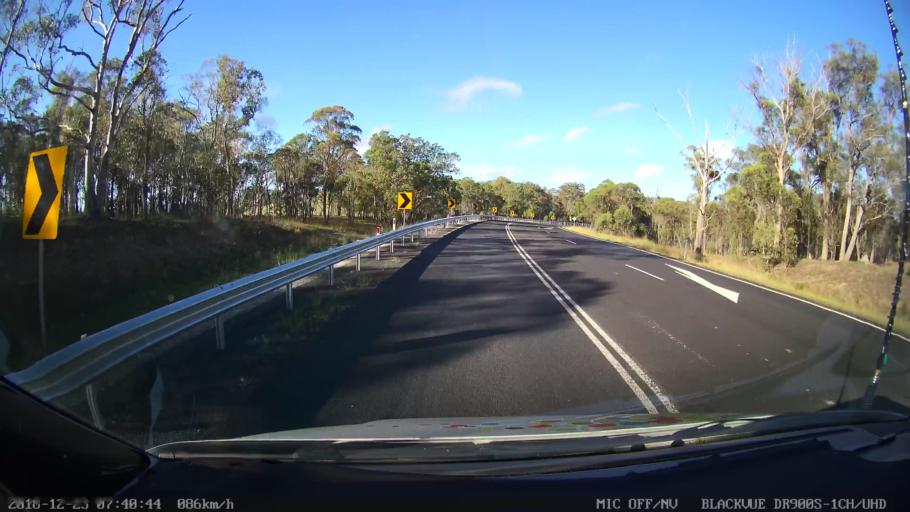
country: AU
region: New South Wales
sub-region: Armidale Dumaresq
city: Enmore
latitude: -30.5153
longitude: 152.0028
